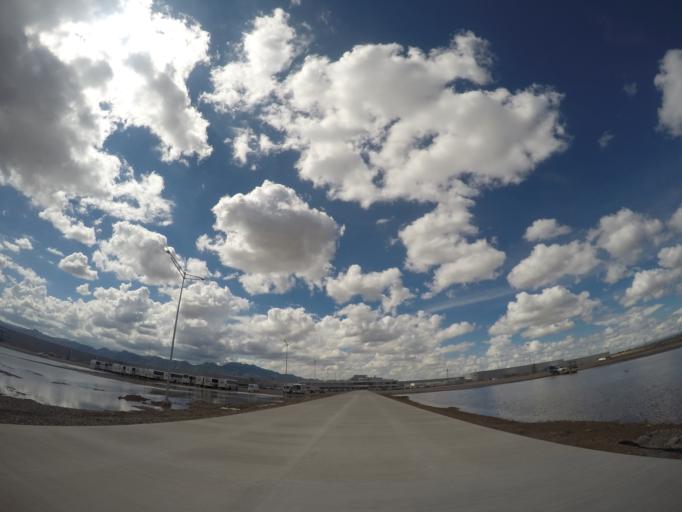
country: MX
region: San Luis Potosi
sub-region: Zaragoza
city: Cerro Gordo
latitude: 21.9654
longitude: -100.8451
